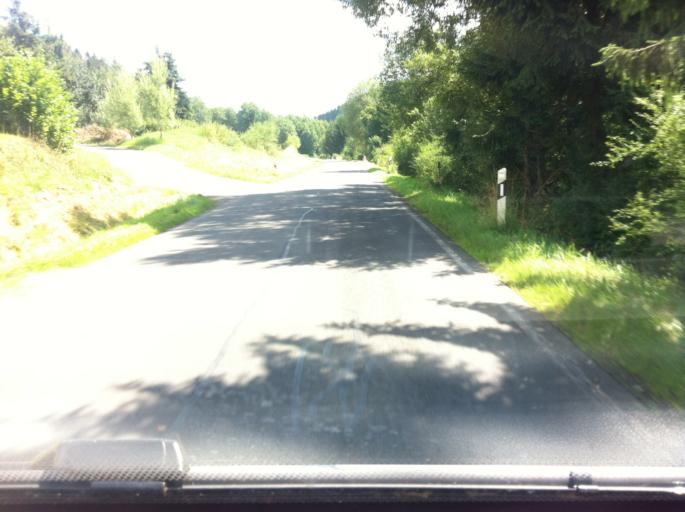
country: DE
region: Rheinland-Pfalz
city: Kalenborn-Scheuern
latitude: 50.2439
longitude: 6.5914
